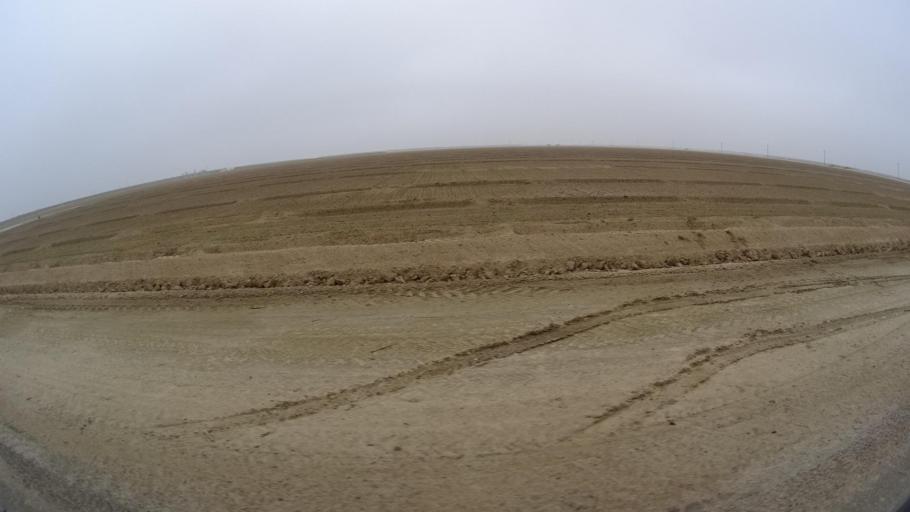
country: US
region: California
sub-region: Kern County
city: Lost Hills
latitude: 35.5910
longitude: -119.5270
